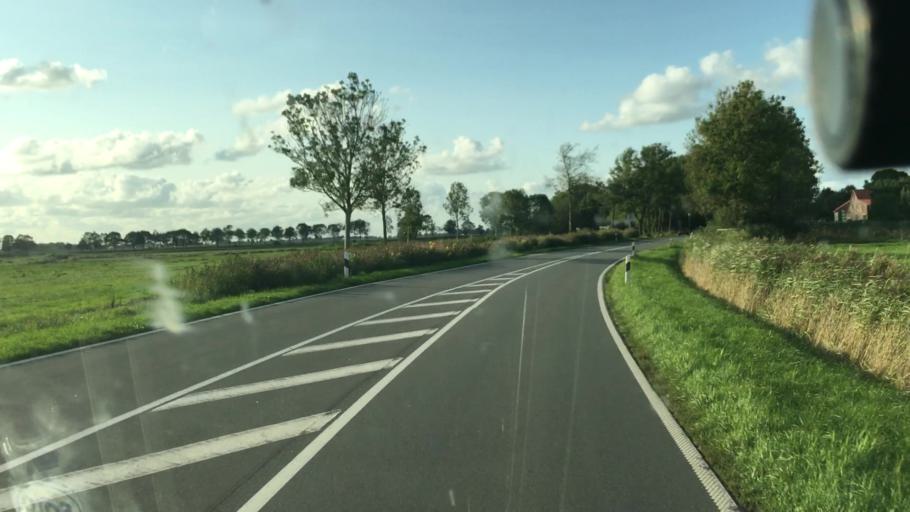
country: DE
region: Lower Saxony
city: Jever
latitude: 53.5938
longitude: 7.8700
